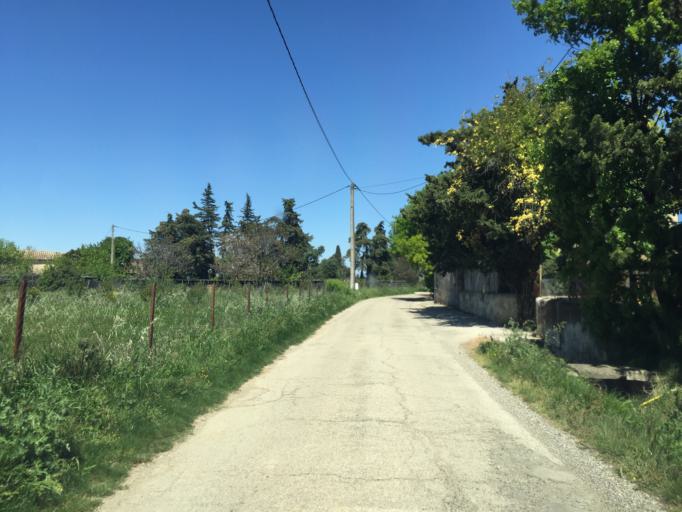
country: FR
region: Provence-Alpes-Cote d'Azur
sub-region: Departement du Vaucluse
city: Jonquieres
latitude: 44.1354
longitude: 4.9140
